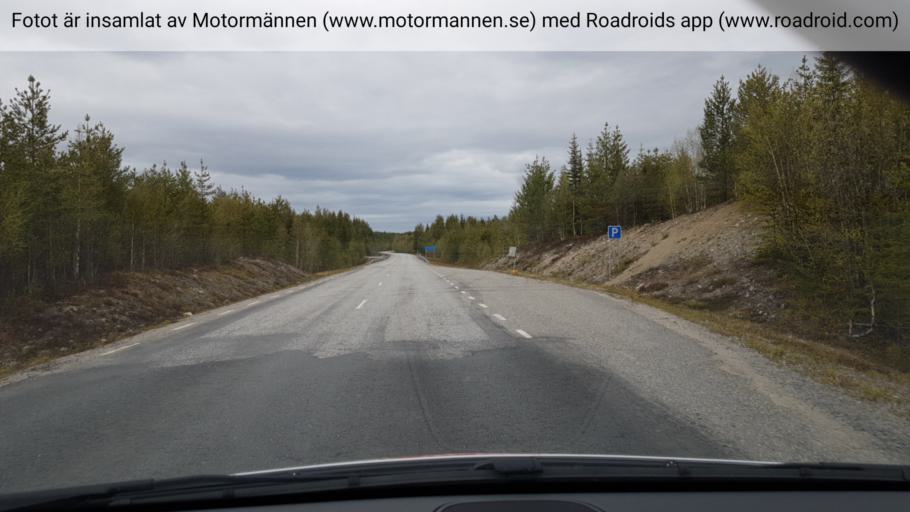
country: SE
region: Vaesterbotten
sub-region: Sorsele Kommun
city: Sorsele
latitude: 65.5165
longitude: 17.3760
